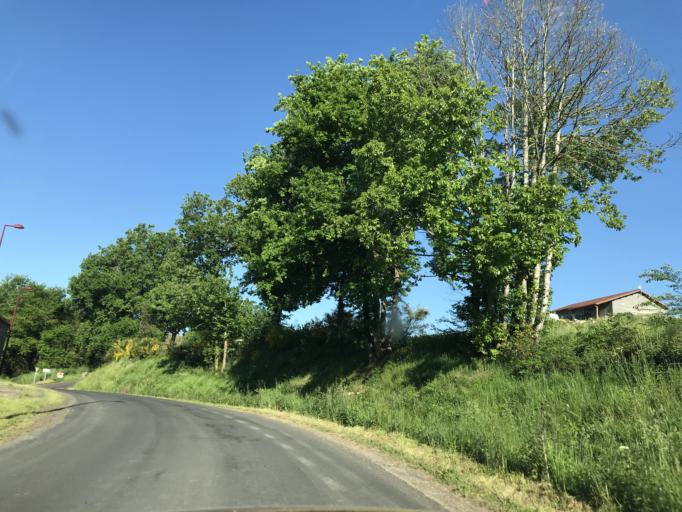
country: FR
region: Auvergne
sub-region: Departement du Puy-de-Dome
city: Job
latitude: 45.6582
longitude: 3.6758
